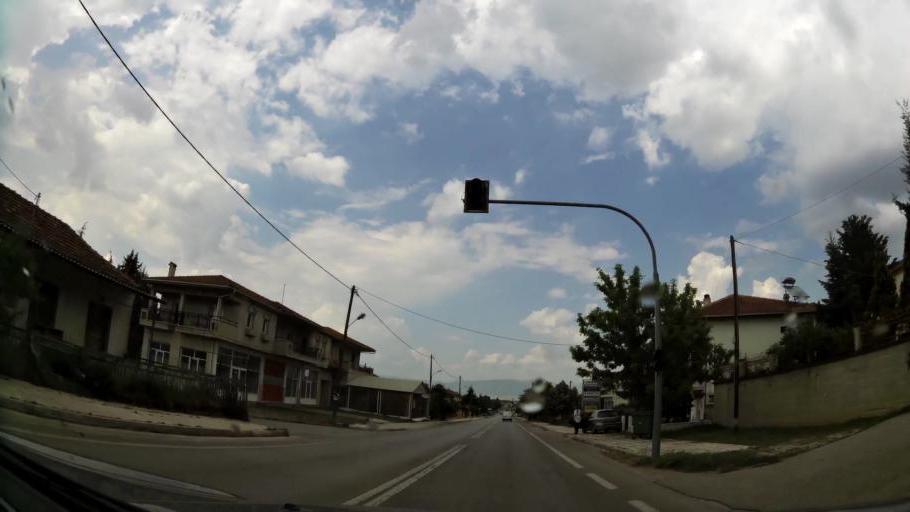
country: GR
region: West Macedonia
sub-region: Nomos Kozanis
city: Koila
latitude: 40.3458
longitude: 21.8264
